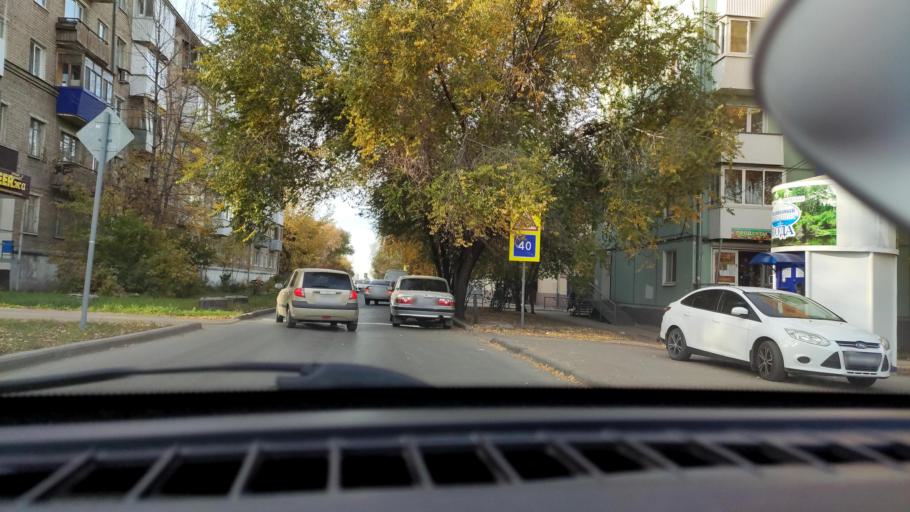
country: RU
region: Samara
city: Samara
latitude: 53.2025
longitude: 50.1604
